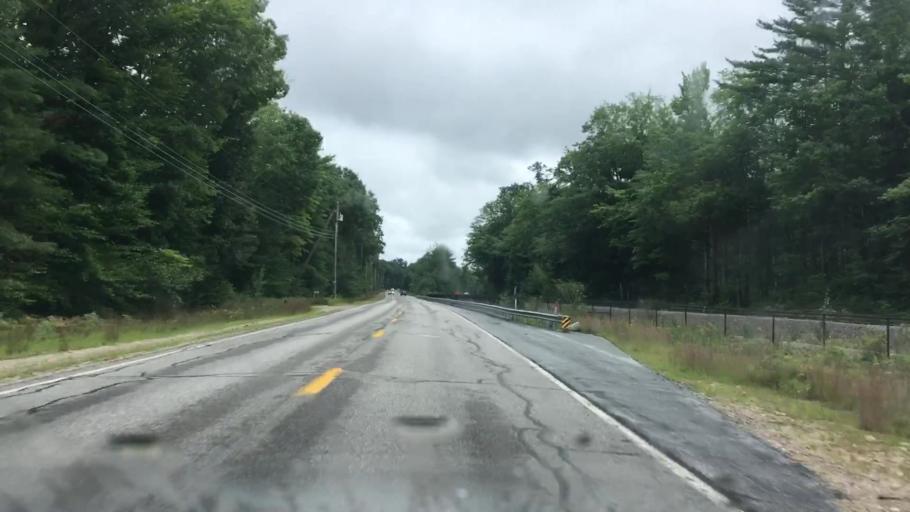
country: US
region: Maine
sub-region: Oxford County
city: Fryeburg
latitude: 44.0073
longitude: -70.9533
